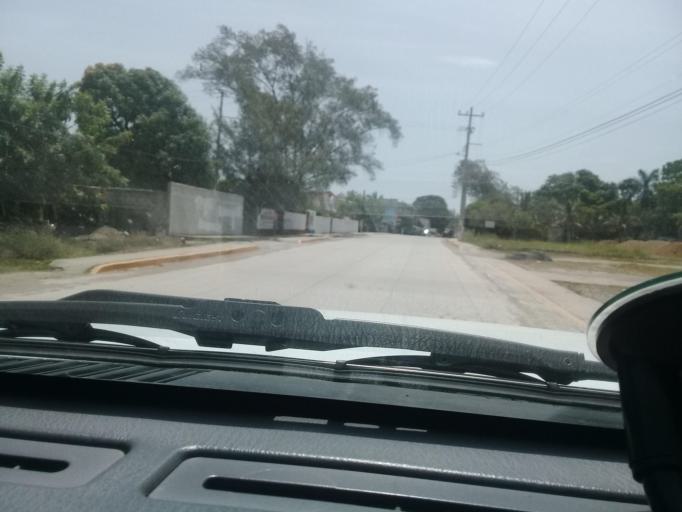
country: MX
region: Veracruz
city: Anahuac
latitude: 22.2291
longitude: -97.8304
